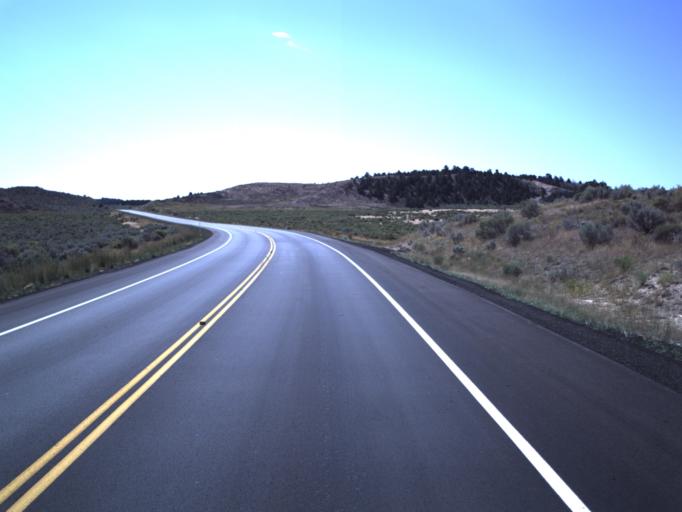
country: US
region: Utah
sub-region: Utah County
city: Eagle Mountain
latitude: 40.0022
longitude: -112.2753
